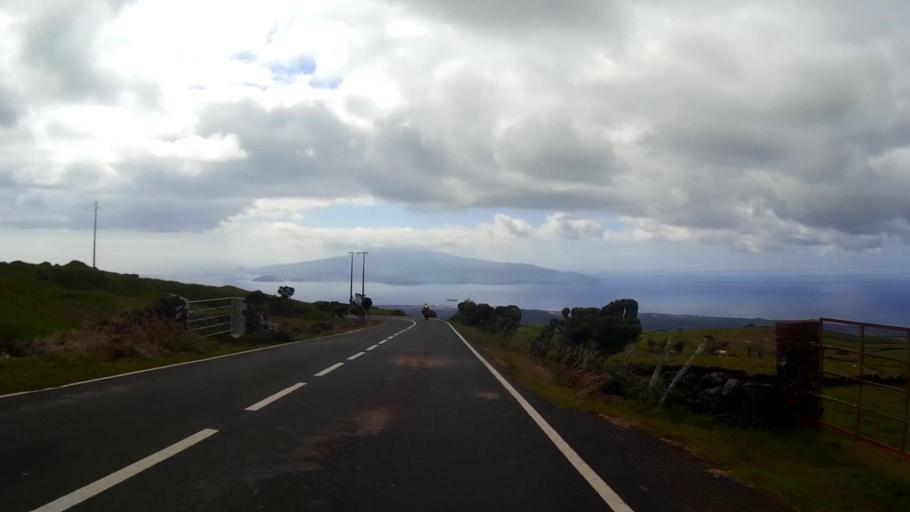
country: PT
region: Azores
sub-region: Madalena
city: Madalena
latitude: 38.4963
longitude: -28.4425
